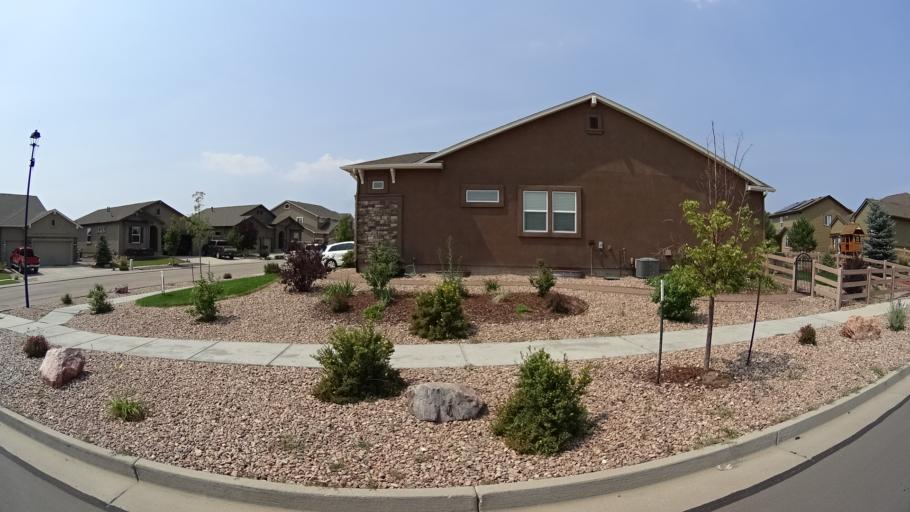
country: US
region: Colorado
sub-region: El Paso County
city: Black Forest
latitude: 38.9698
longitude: -104.7157
